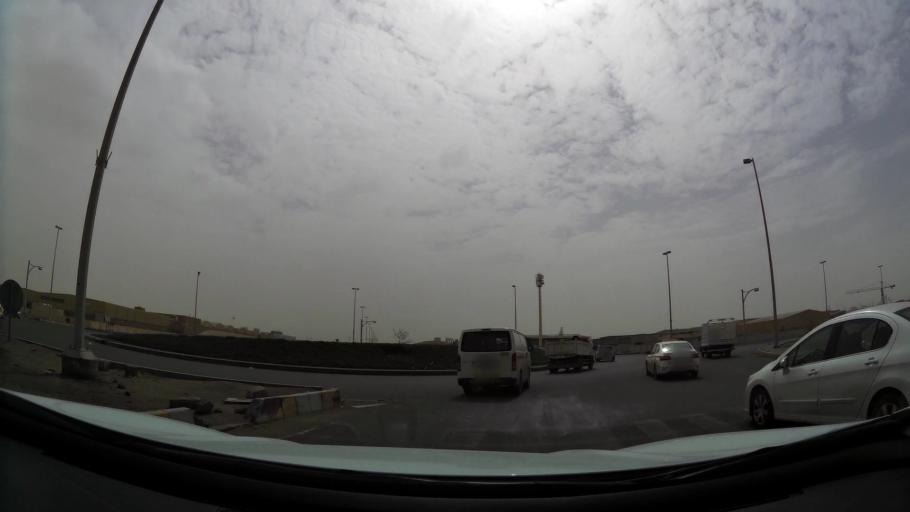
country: AE
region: Abu Dhabi
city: Abu Dhabi
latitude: 24.3451
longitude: 54.4728
